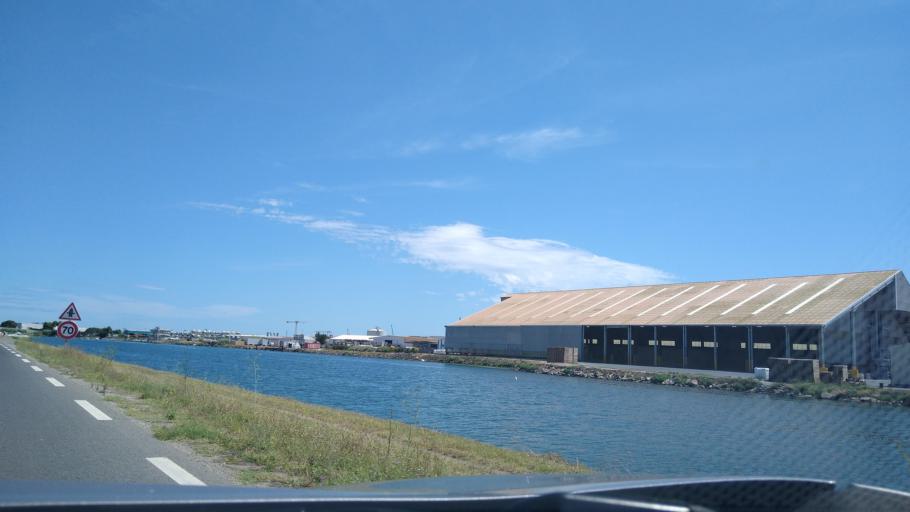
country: FR
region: Languedoc-Roussillon
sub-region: Departement de l'Herault
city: Sete
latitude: 43.4230
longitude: 3.7130
